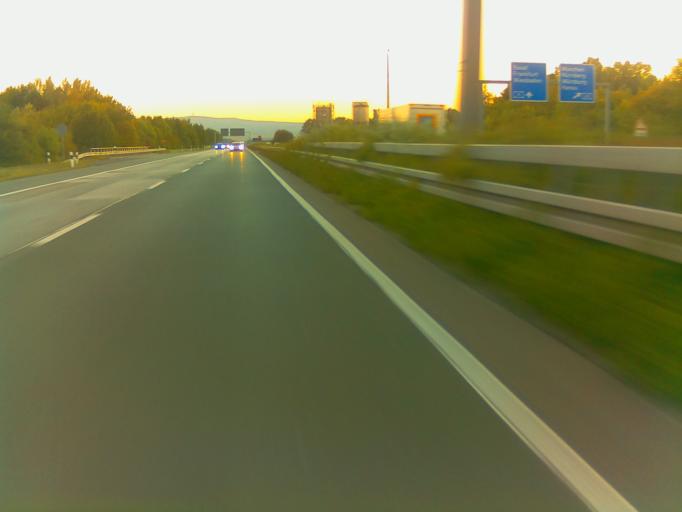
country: DE
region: Hesse
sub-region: Regierungsbezirk Darmstadt
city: Rockenberg
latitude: 50.4755
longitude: 8.7275
